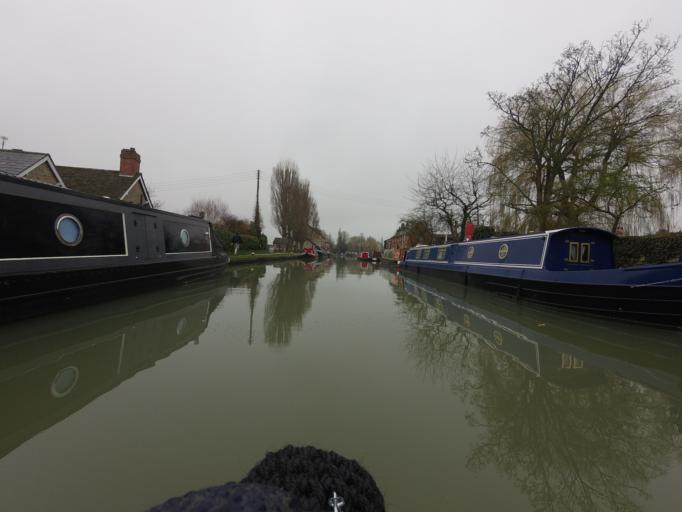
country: GB
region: England
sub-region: Northamptonshire
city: Roade
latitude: 52.1432
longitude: -0.9162
